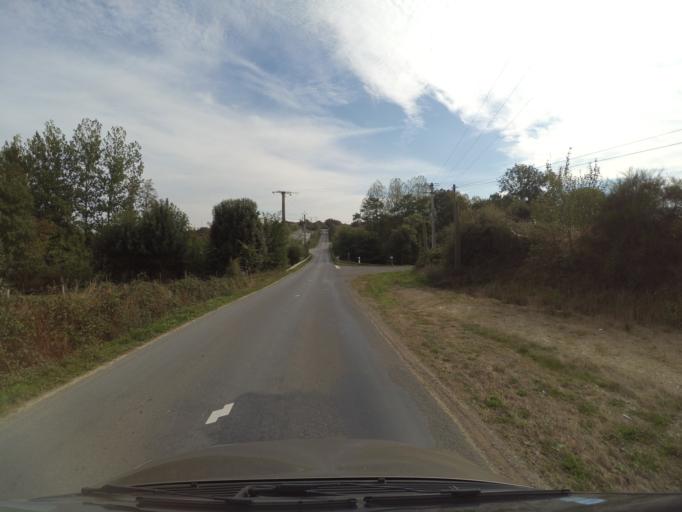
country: FR
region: Pays de la Loire
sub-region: Departement de Maine-et-Loire
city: Villedieu-la-Blouere
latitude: 47.1546
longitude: -1.0462
